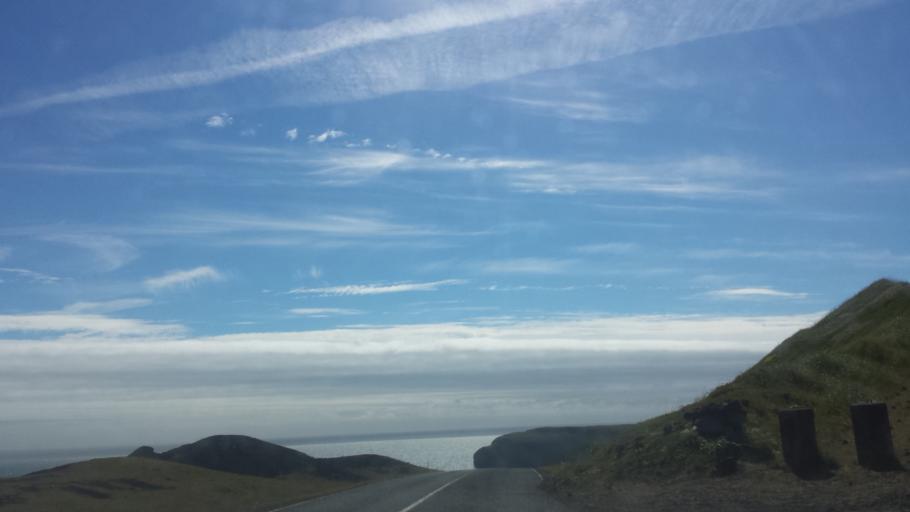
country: IS
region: South
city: Vestmannaeyjar
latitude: 63.4288
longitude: -20.2557
